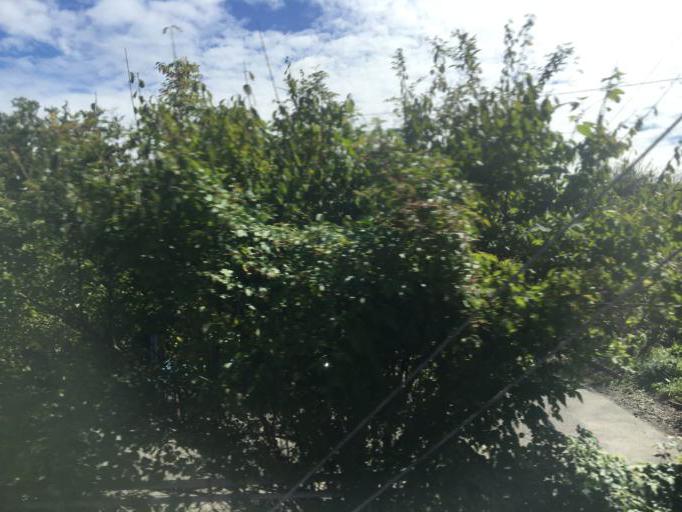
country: JP
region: Akita
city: Akita
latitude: 39.6972
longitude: 140.1189
